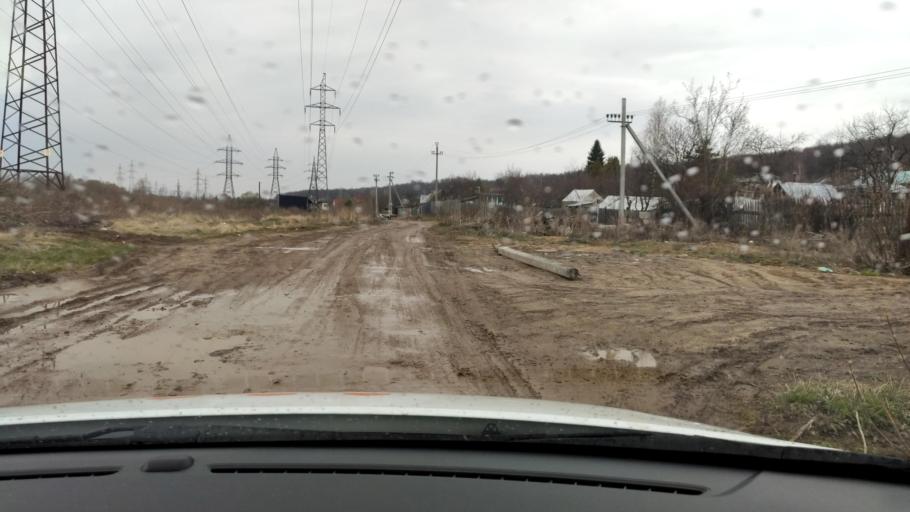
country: RU
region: Tatarstan
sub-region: Gorod Kazan'
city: Kazan
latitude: 55.8180
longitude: 49.2110
